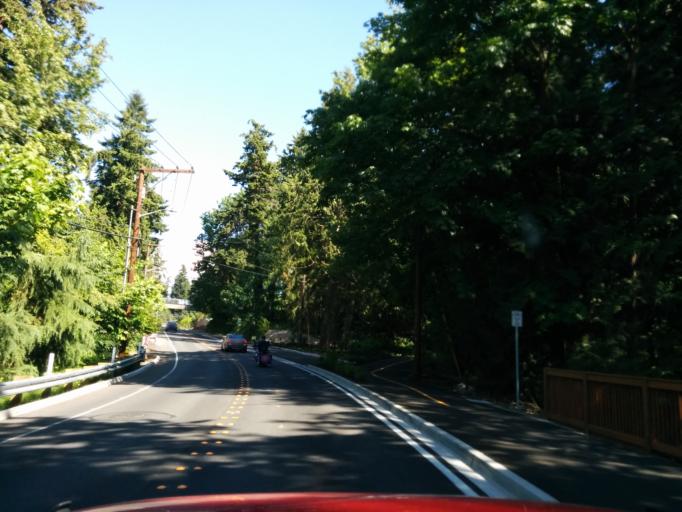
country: US
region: Washington
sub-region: King County
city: West Lake Sammamish
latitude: 47.5717
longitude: -122.1066
